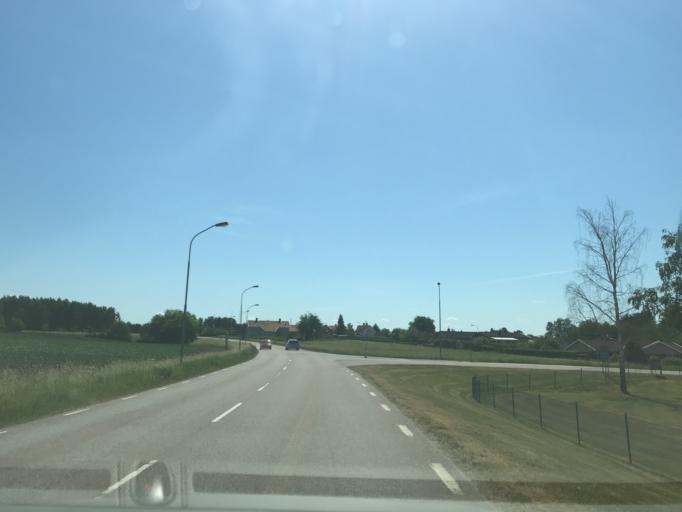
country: SE
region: Vaestra Goetaland
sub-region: Gotene Kommun
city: Kallby
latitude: 58.5085
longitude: 13.3116
